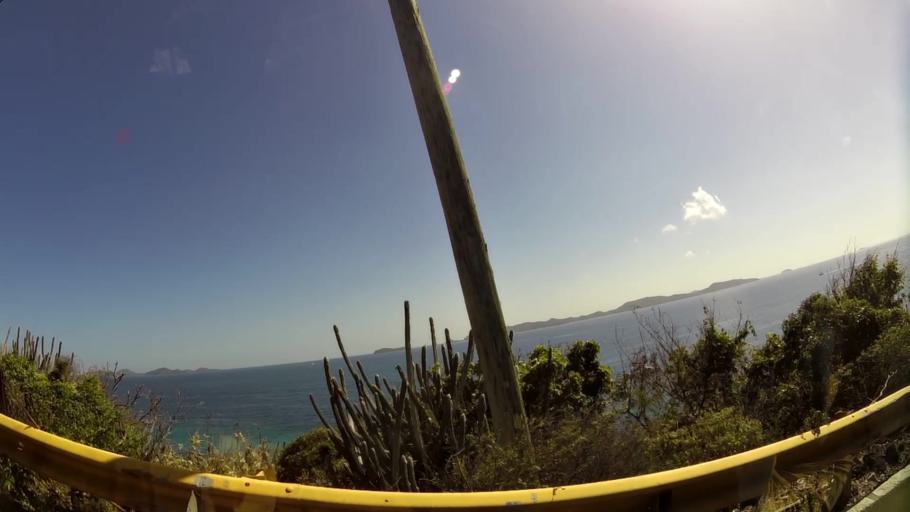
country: VG
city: Tortola
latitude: 18.4122
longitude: -64.5910
